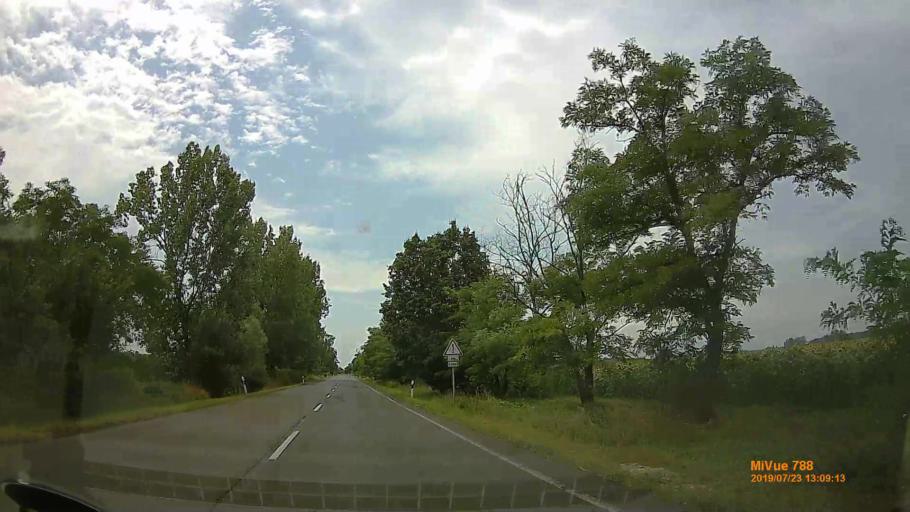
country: HU
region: Szabolcs-Szatmar-Bereg
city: Tiszavasvari
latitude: 47.9391
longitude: 21.3103
